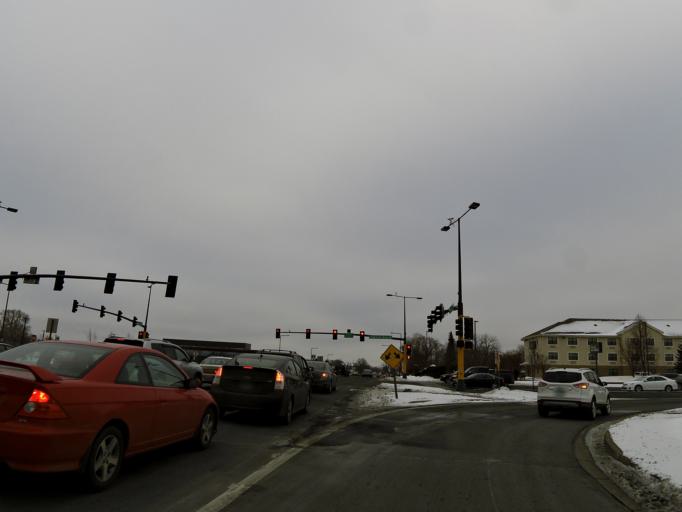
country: US
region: Minnesota
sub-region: Hennepin County
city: Bloomington
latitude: 44.8597
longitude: -93.2886
